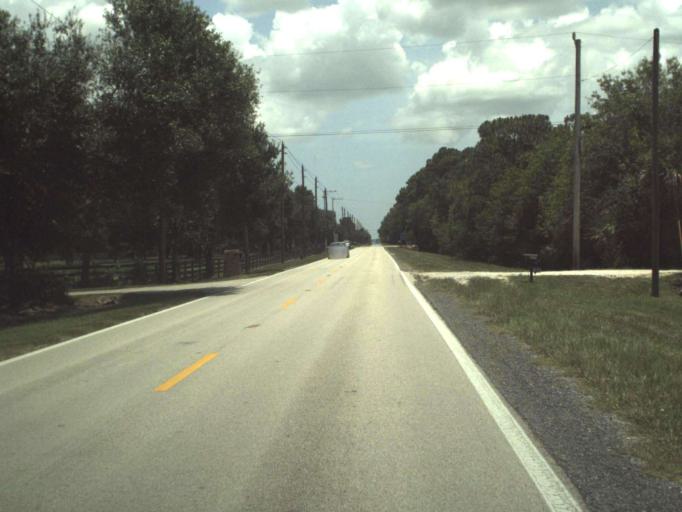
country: US
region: Florida
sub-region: Saint Lucie County
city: Fort Pierce South
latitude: 27.3744
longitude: -80.4345
